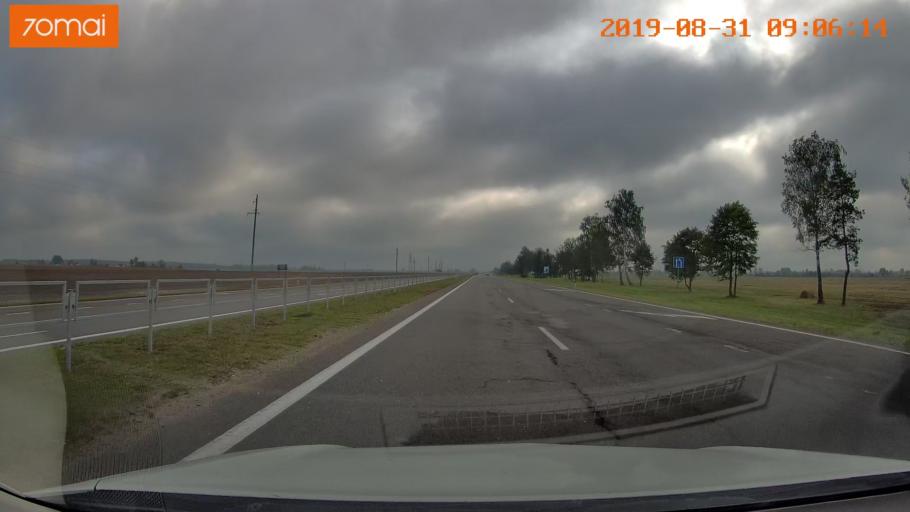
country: BY
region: Minsk
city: Chervyen'
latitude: 53.7245
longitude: 28.4002
